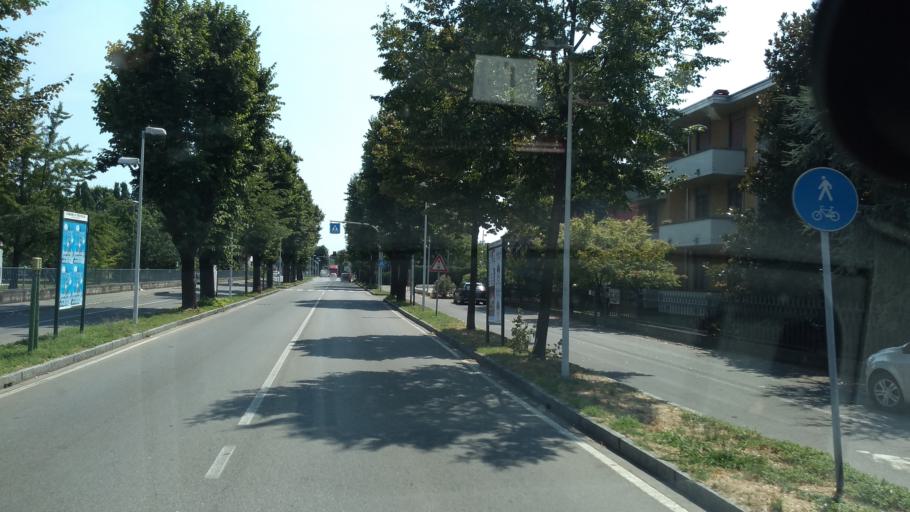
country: IT
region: Lombardy
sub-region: Provincia di Bergamo
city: Treviglio
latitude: 45.5203
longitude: 9.5836
